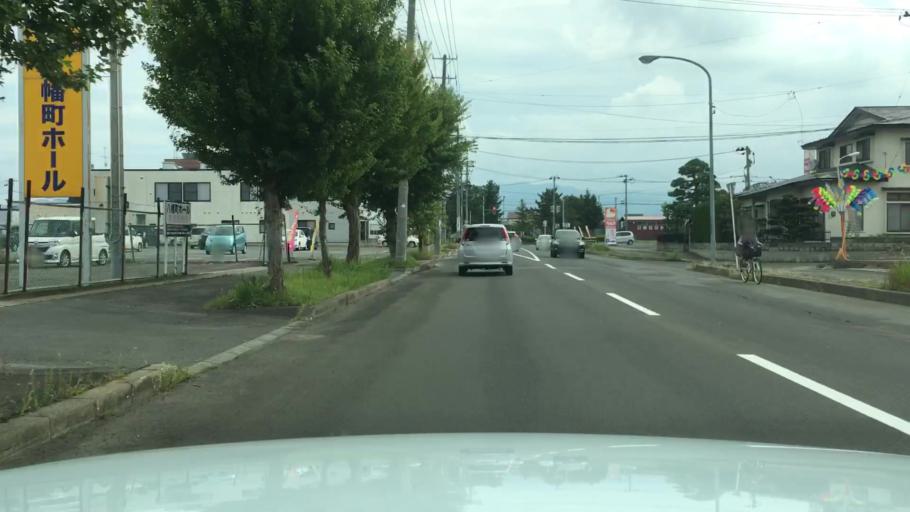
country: JP
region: Aomori
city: Hirosaki
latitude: 40.6187
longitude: 140.4844
